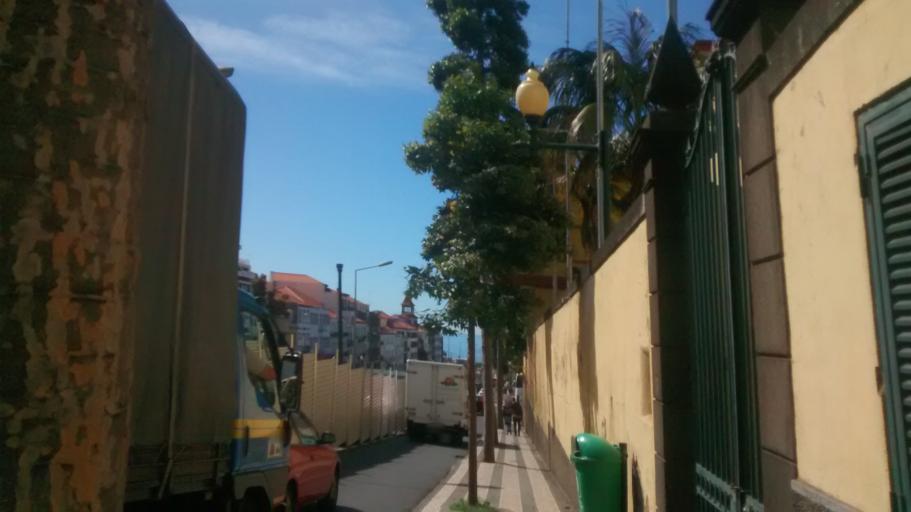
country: PT
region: Madeira
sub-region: Funchal
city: Nossa Senhora do Monte
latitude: 32.6514
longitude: -16.9089
